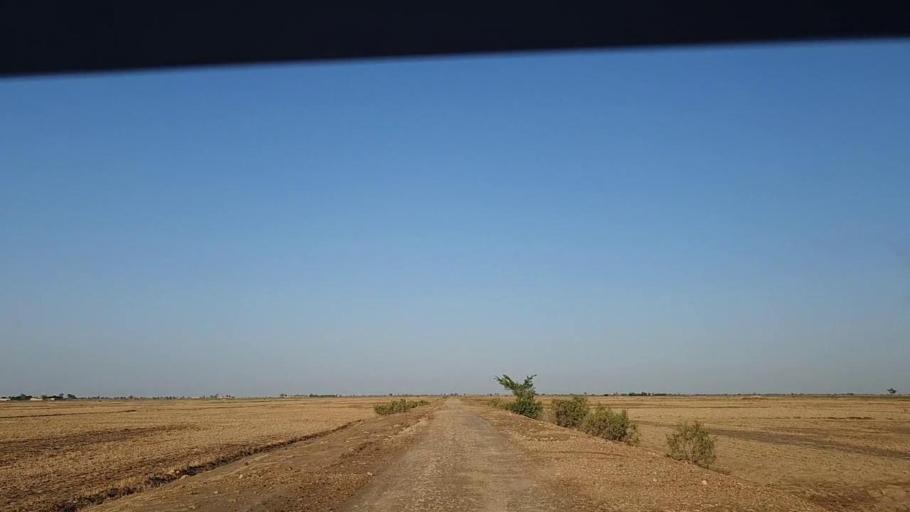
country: PK
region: Sindh
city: Johi
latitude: 26.7444
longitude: 67.6193
